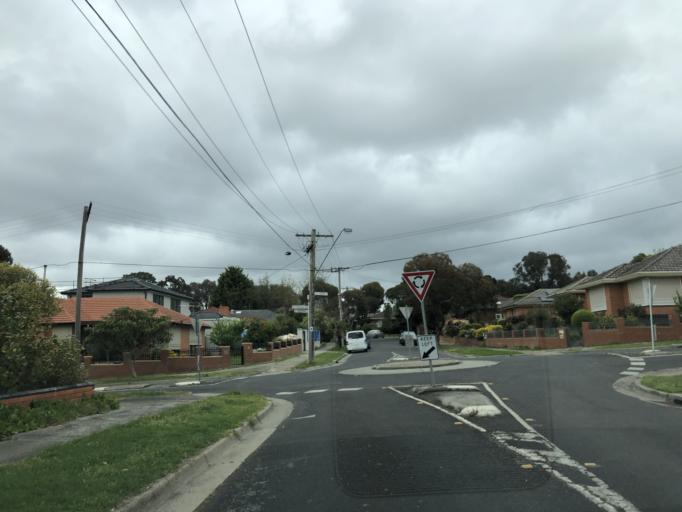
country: AU
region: Victoria
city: Burwood East
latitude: -37.8538
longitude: 145.1412
